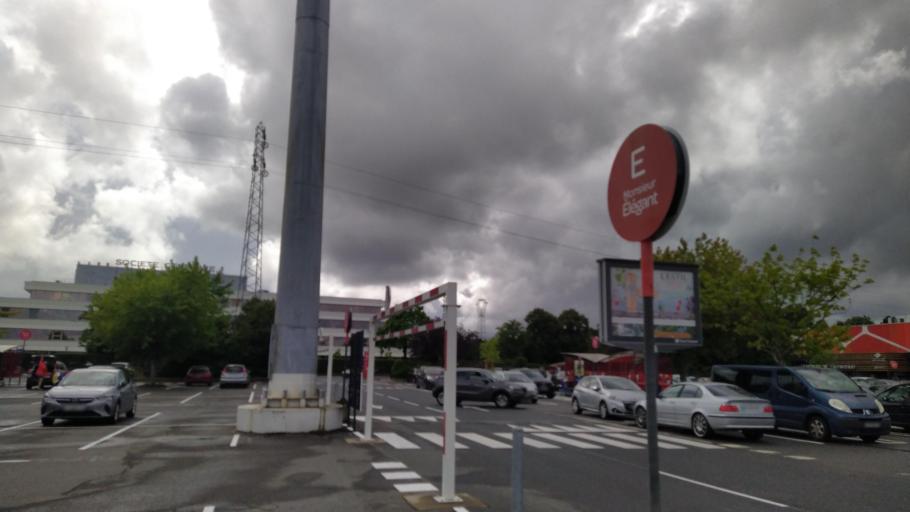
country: FR
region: Pays de la Loire
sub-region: Departement de la Loire-Atlantique
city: Sainte-Luce-sur-Loire
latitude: 47.2568
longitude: -1.5121
